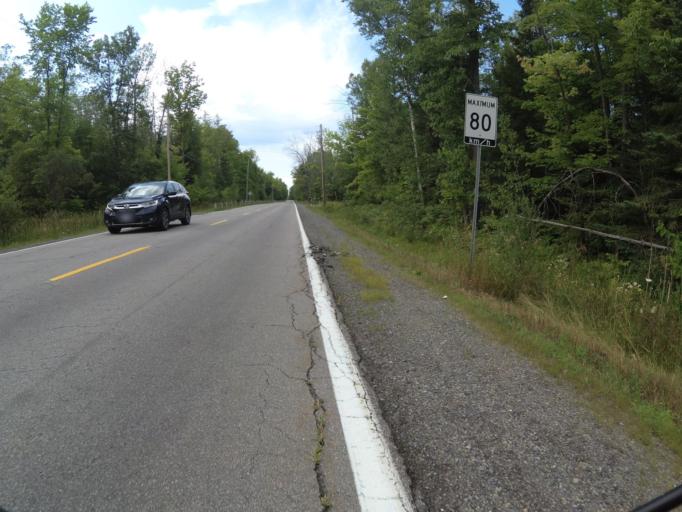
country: CA
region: Ontario
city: Arnprior
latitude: 45.4865
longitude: -76.1079
